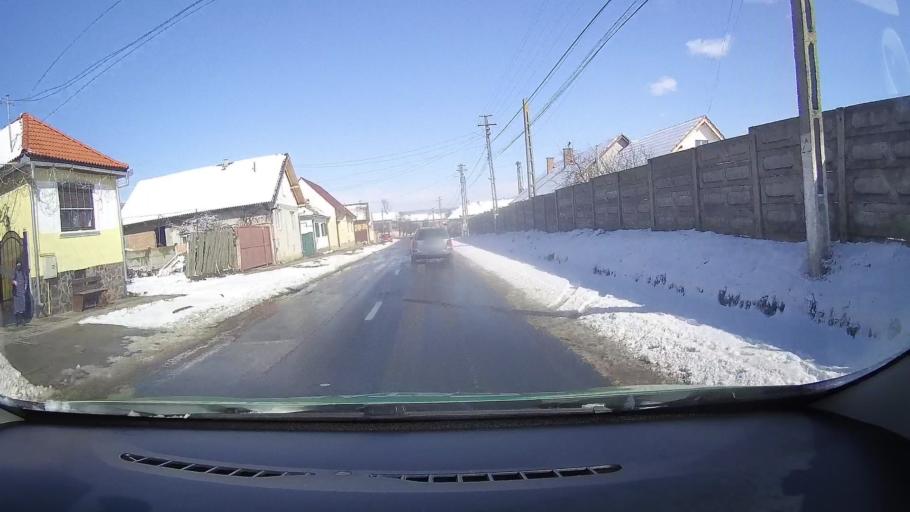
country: RO
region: Sibiu
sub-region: Comuna Rosia
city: Rosia
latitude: 45.8155
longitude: 24.3085
